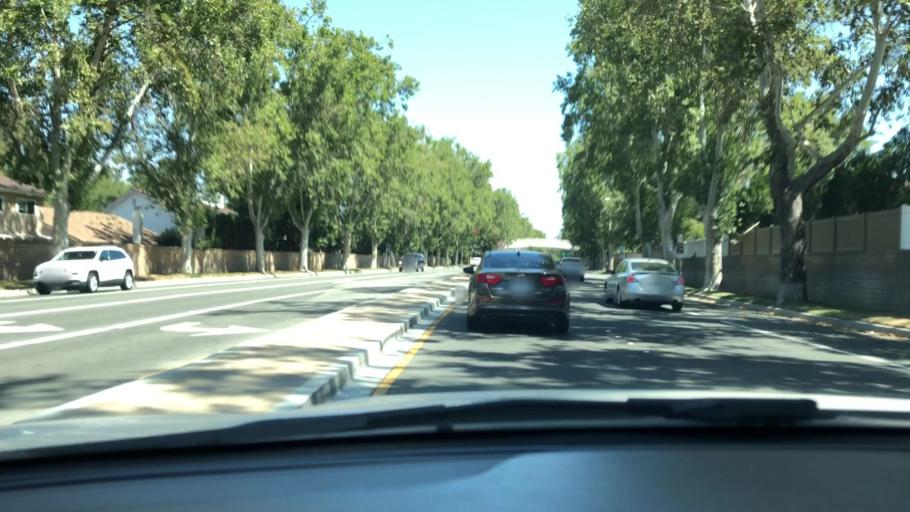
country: US
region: California
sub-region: Los Angeles County
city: Santa Clarita
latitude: 34.3958
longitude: -118.5527
